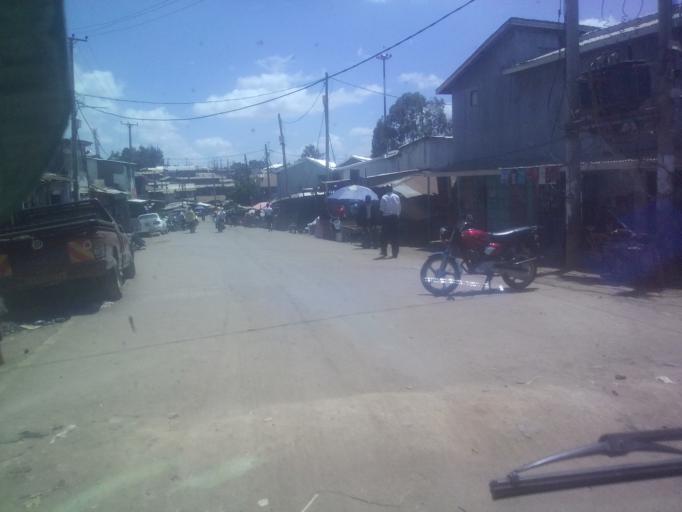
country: KE
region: Nairobi Area
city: Nairobi
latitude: -1.3121
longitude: 36.7922
